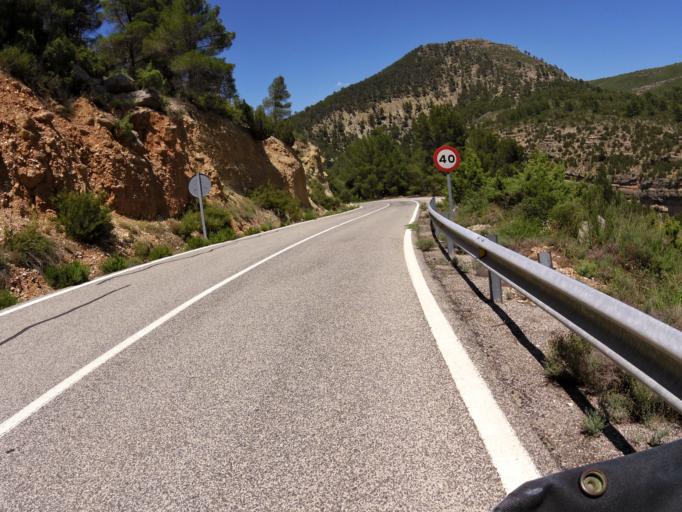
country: ES
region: Valencia
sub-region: Provincia de Valencia
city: Casas Bajas
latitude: 39.9846
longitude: -1.2763
